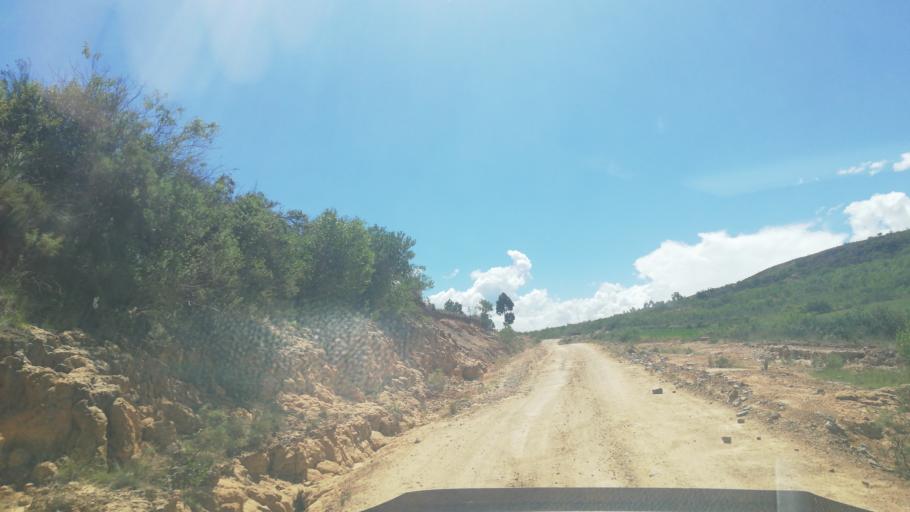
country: BO
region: Cochabamba
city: Totora
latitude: -17.7373
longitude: -65.2215
